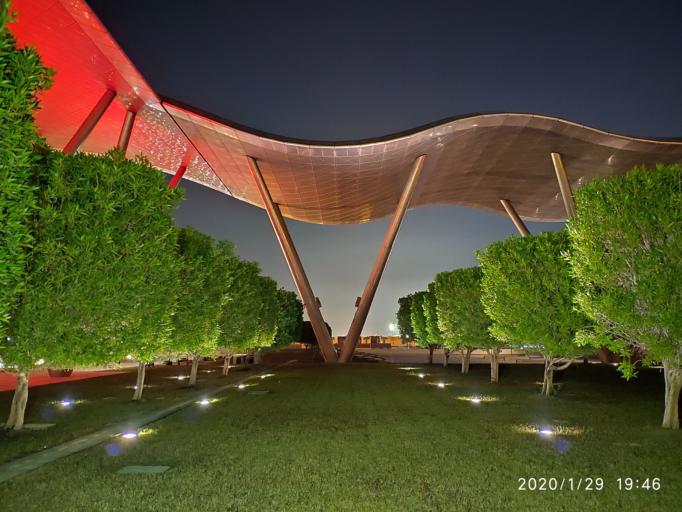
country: QA
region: Baladiyat ar Rayyan
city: Ar Rayyan
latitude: 25.3258
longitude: 51.4378
